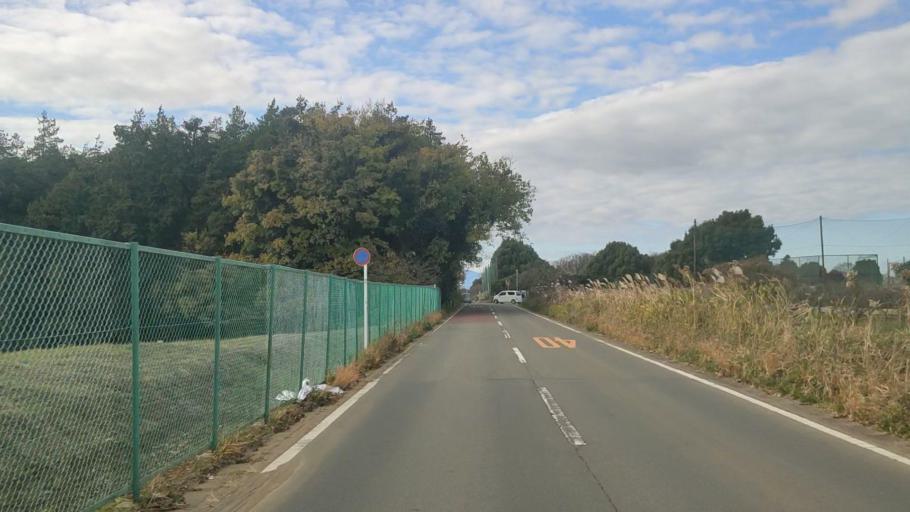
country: JP
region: Kanagawa
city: Minami-rinkan
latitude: 35.4843
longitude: 139.4852
